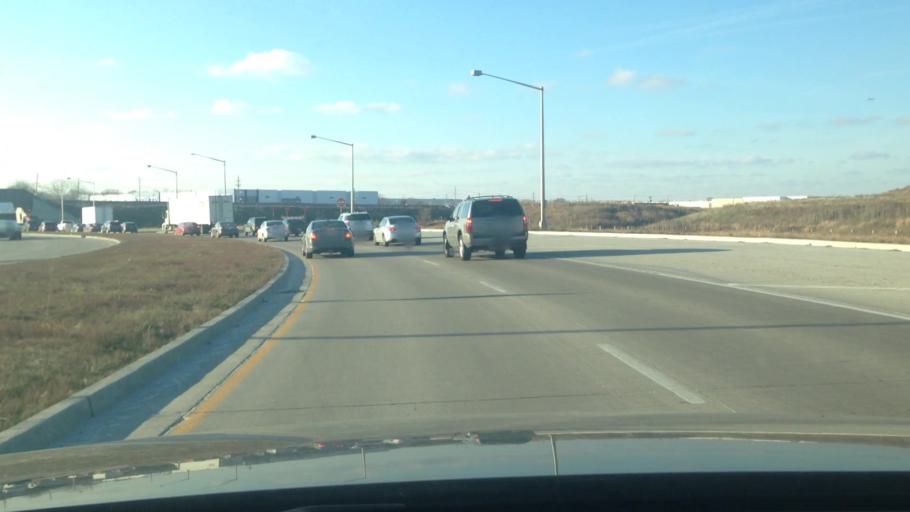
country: US
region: Illinois
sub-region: DuPage County
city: Bensenville
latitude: 41.9604
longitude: -87.9352
